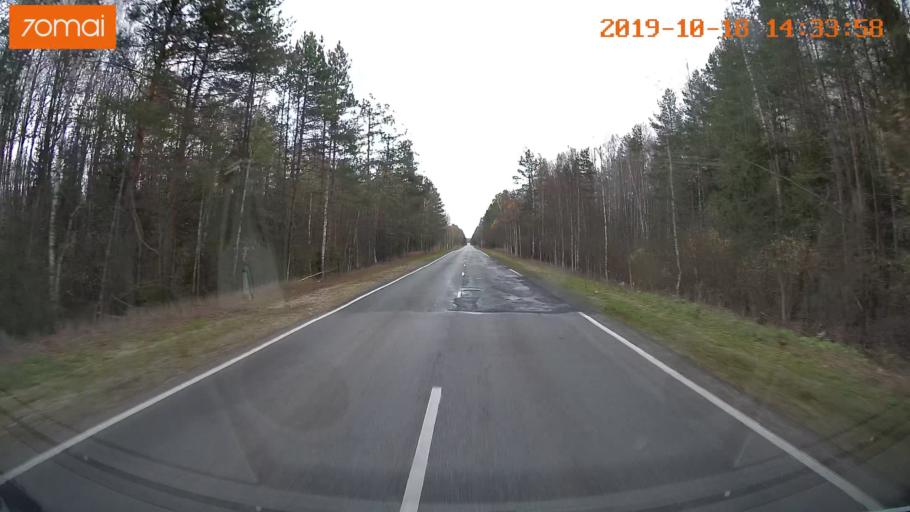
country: RU
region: Vladimir
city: Velikodvorskiy
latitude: 55.2072
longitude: 40.6070
